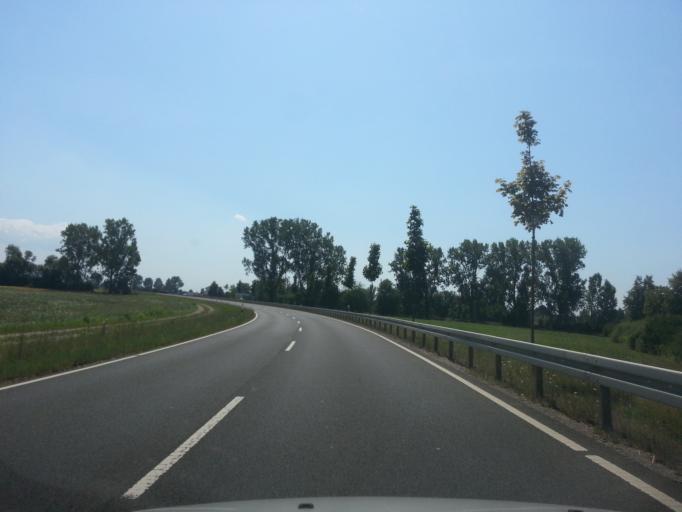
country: DE
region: Hesse
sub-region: Regierungsbezirk Darmstadt
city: Biblis
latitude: 49.6697
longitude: 8.4509
